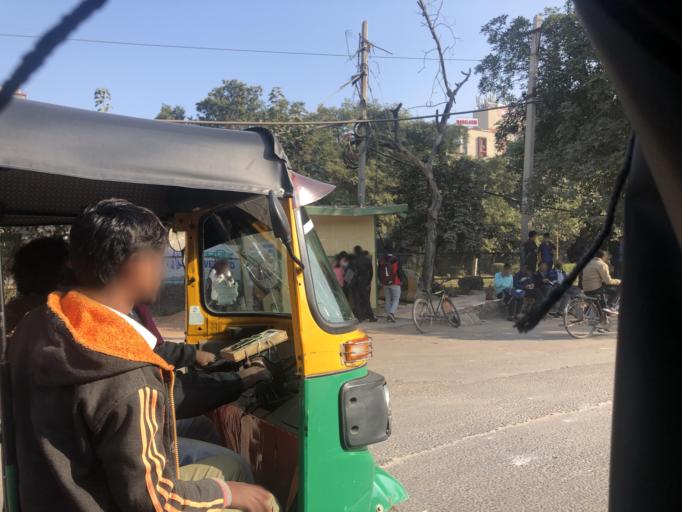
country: IN
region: Haryana
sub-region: Gurgaon
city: Gurgaon
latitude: 28.4583
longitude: 77.0742
